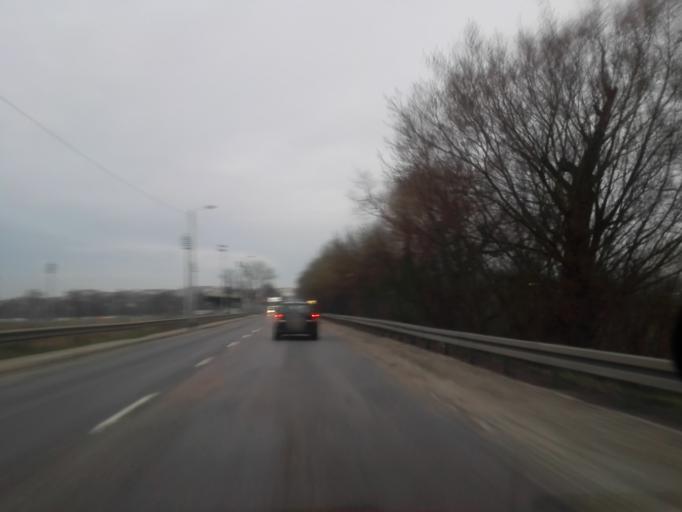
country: PL
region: Podlasie
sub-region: Powiat lomzynski
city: Piatnica
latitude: 53.1897
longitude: 22.0896
